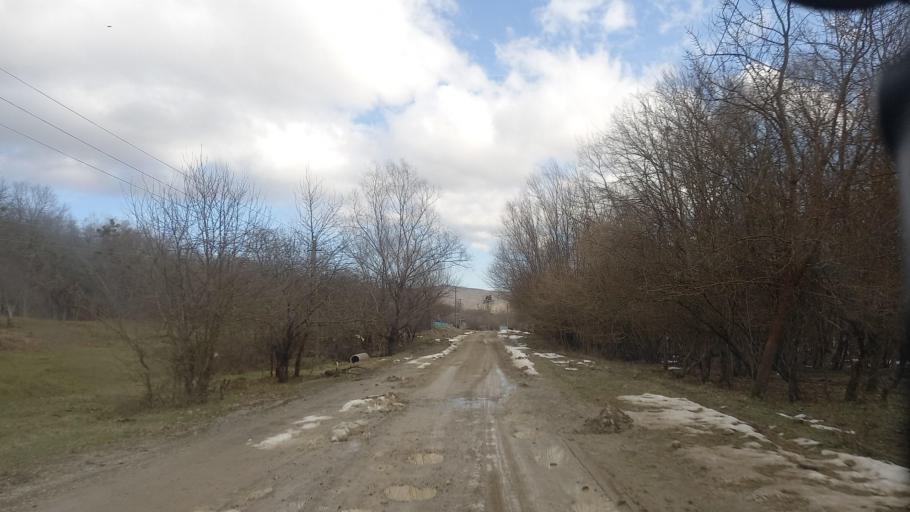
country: RU
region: Krasnodarskiy
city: Smolenskaya
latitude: 44.6028
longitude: 38.8647
